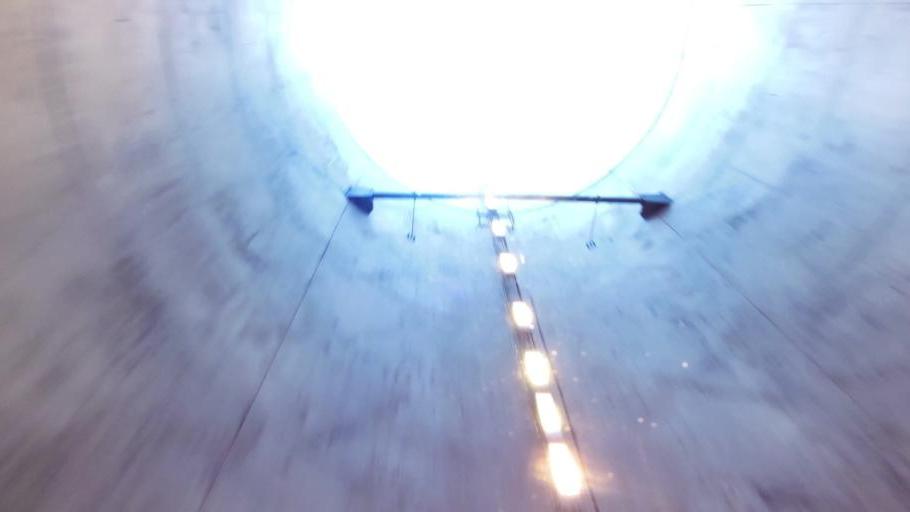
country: IS
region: Westfjords
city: Isafjoerdur
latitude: 66.1433
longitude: -23.2242
